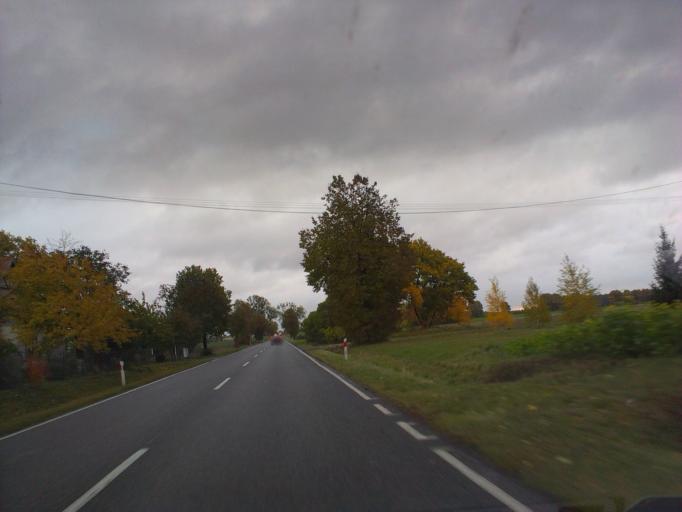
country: PL
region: Kujawsko-Pomorskie
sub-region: Powiat swiecki
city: Bukowiec
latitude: 53.4503
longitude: 18.2360
